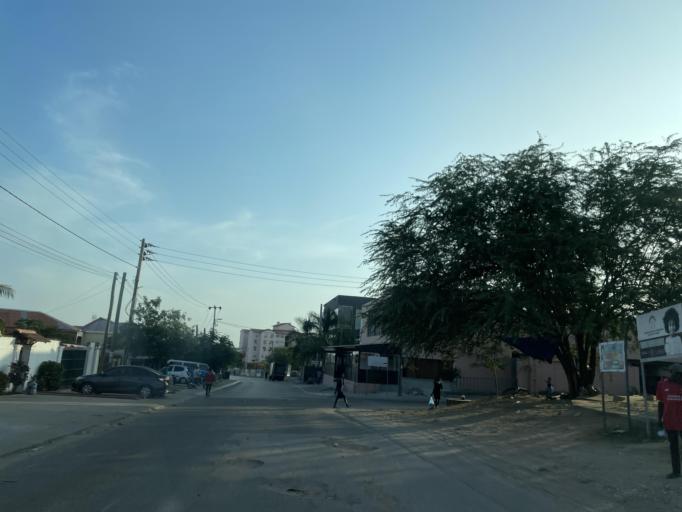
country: AO
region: Luanda
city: Luanda
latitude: -8.9126
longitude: 13.2246
